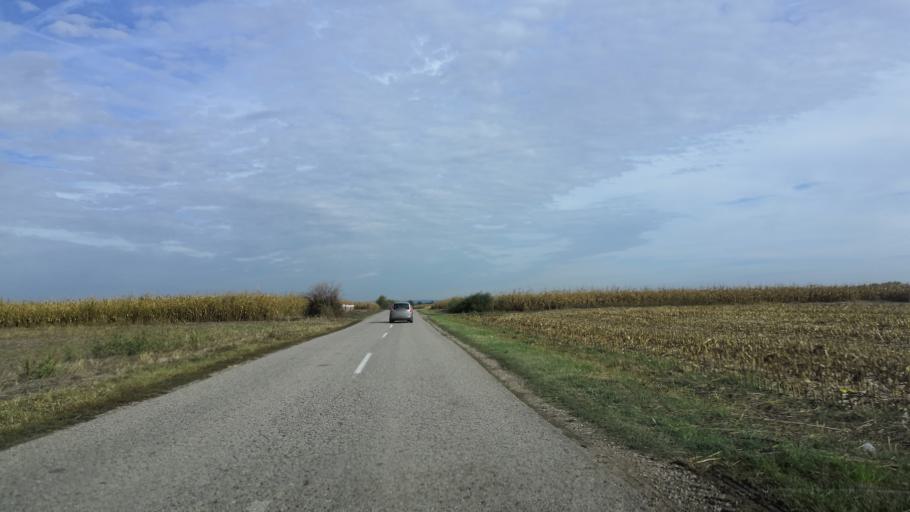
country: RS
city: Novi Karlovci
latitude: 45.0563
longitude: 20.1785
